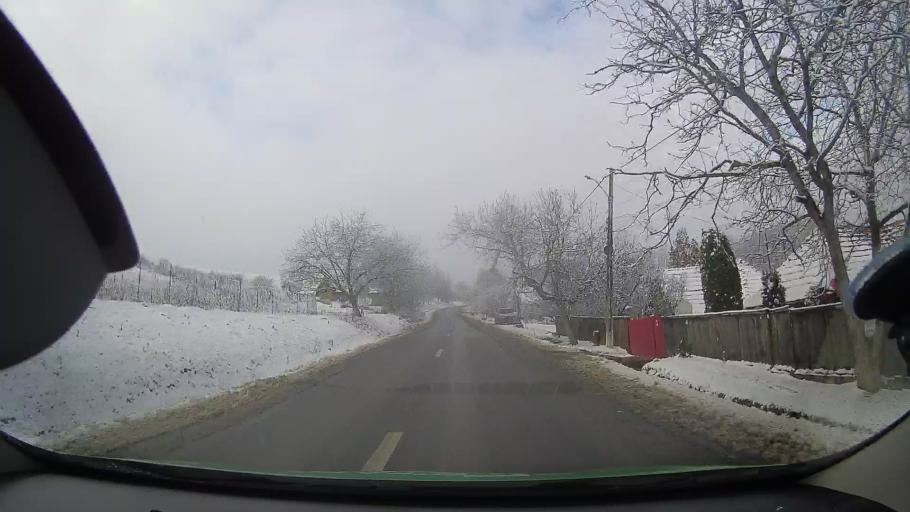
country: RO
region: Mures
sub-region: Comuna Atintis
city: Atintis
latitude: 46.4343
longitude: 24.0978
